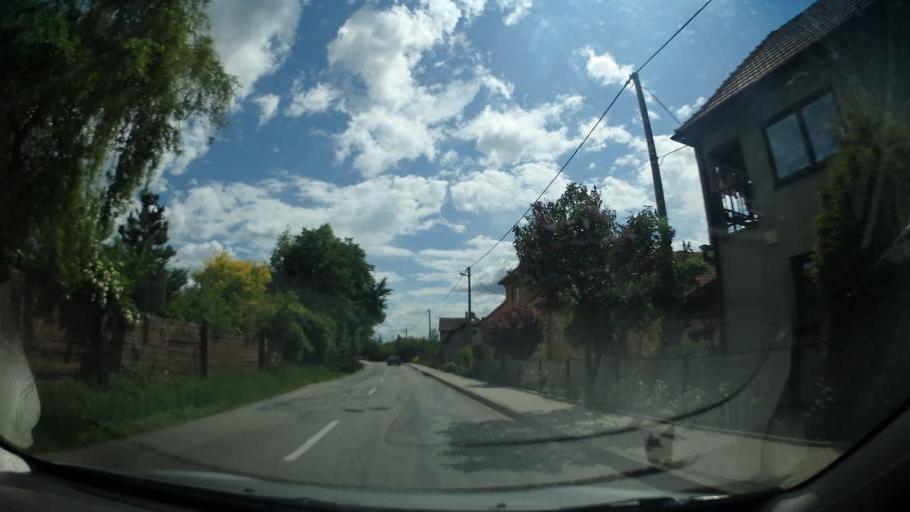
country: CZ
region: South Moravian
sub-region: Okres Blansko
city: Letovice
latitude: 49.5935
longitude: 16.5951
